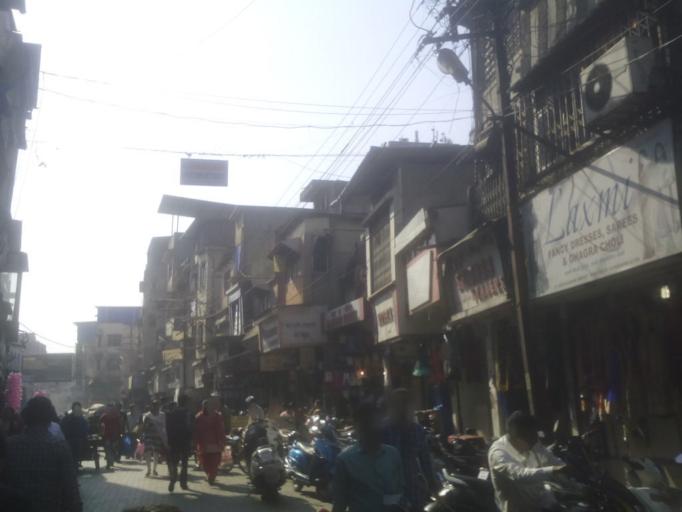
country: IN
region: Maharashtra
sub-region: Thane
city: Ulhasnagar
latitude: 19.2339
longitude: 73.1627
